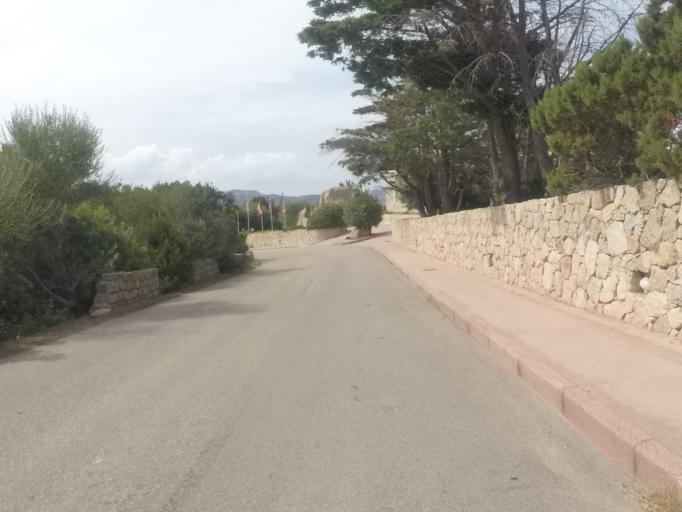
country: IT
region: Sardinia
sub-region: Provincia di Olbia-Tempio
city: Porto Cervo
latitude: 41.1391
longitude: 9.4695
